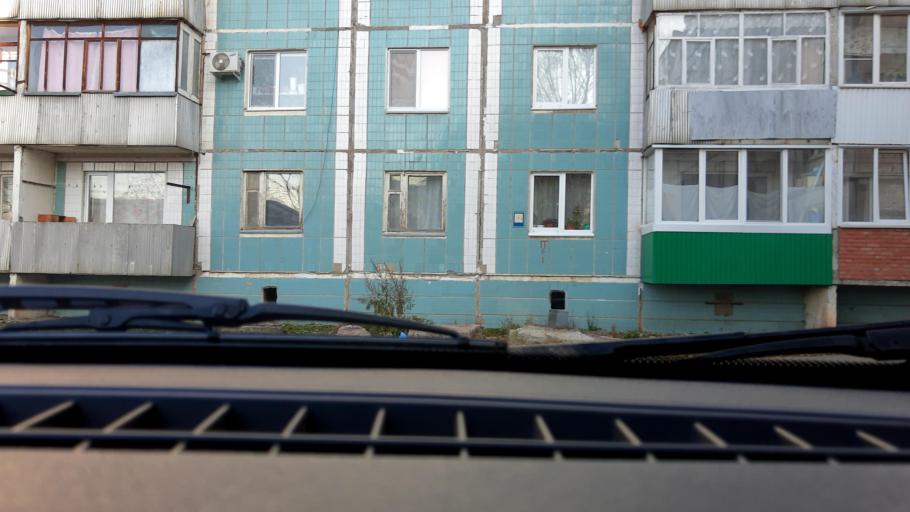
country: RU
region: Bashkortostan
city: Mikhaylovka
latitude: 54.7932
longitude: 55.8632
